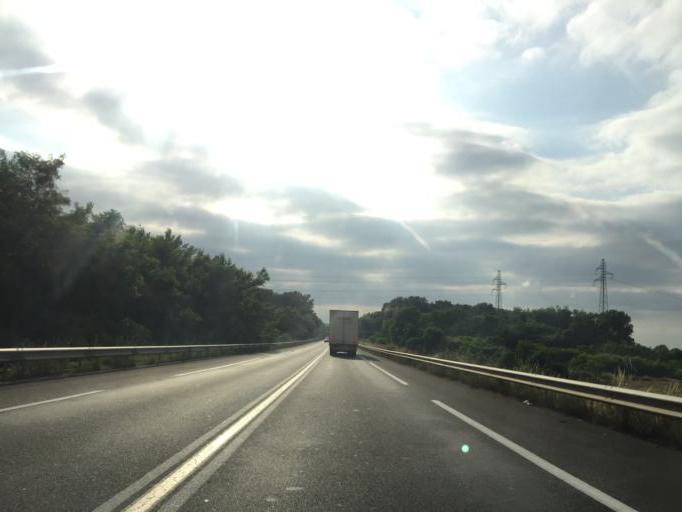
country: FR
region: Auvergne
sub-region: Departement de l'Allier
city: Dompierre-sur-Besbre
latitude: 46.5362
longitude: 3.7036
